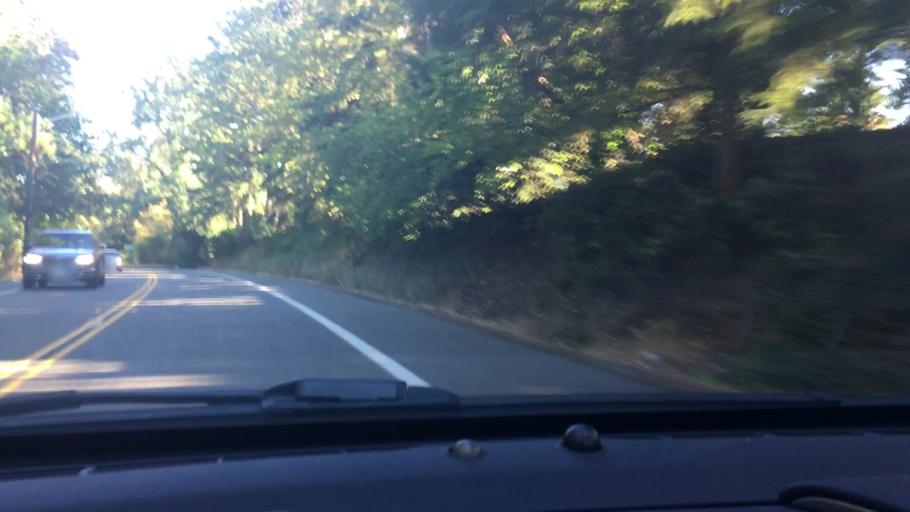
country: US
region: Washington
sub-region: King County
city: West Lake Sammamish
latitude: 47.5907
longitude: -122.0850
